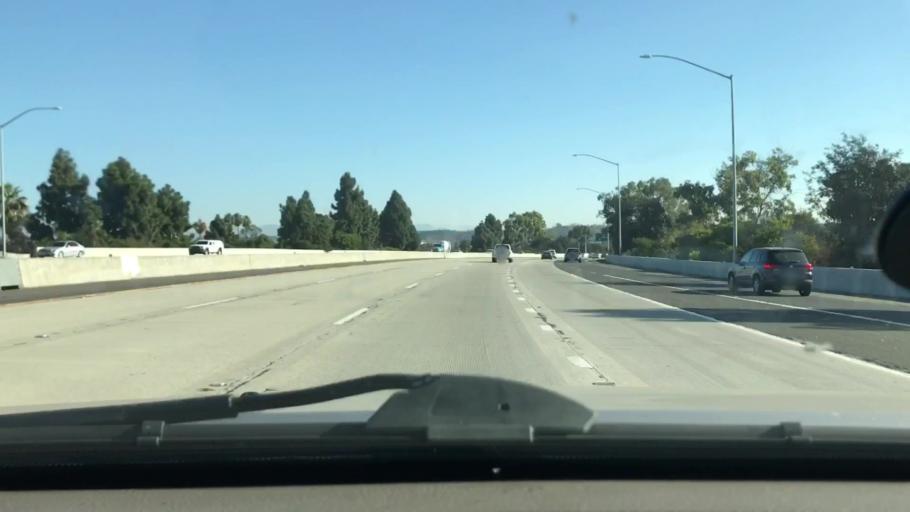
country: US
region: California
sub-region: Los Angeles County
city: Ladera Heights
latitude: 33.9867
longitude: -118.4118
